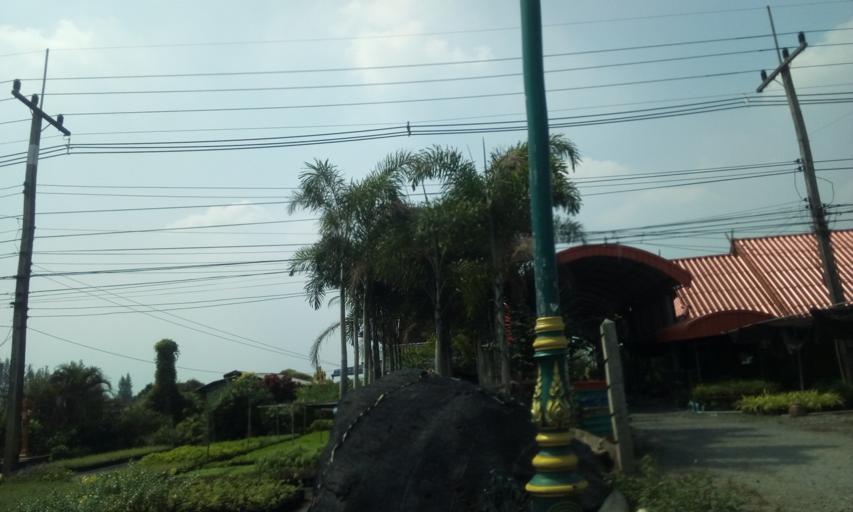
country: TH
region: Nakhon Nayok
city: Ongkharak
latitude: 14.1214
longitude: 100.9431
